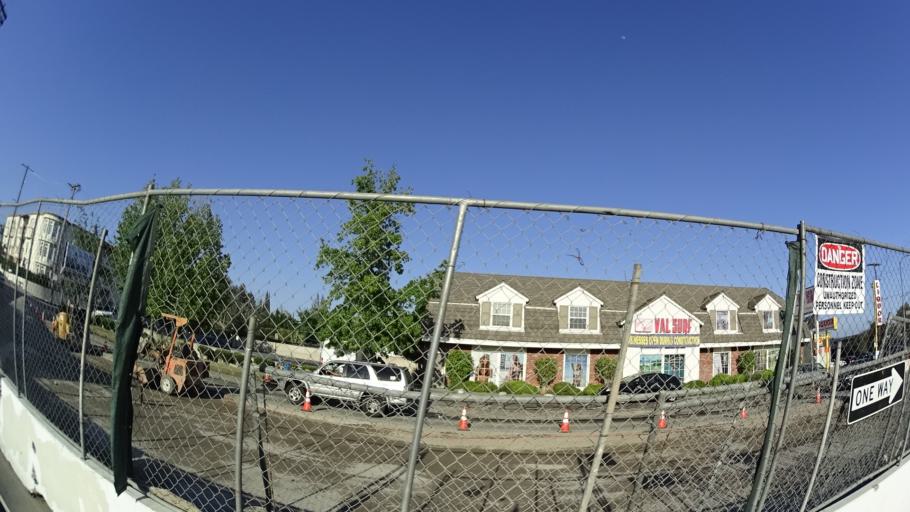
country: US
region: California
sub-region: Los Angeles County
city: North Hollywood
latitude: 34.1582
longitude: -118.4053
